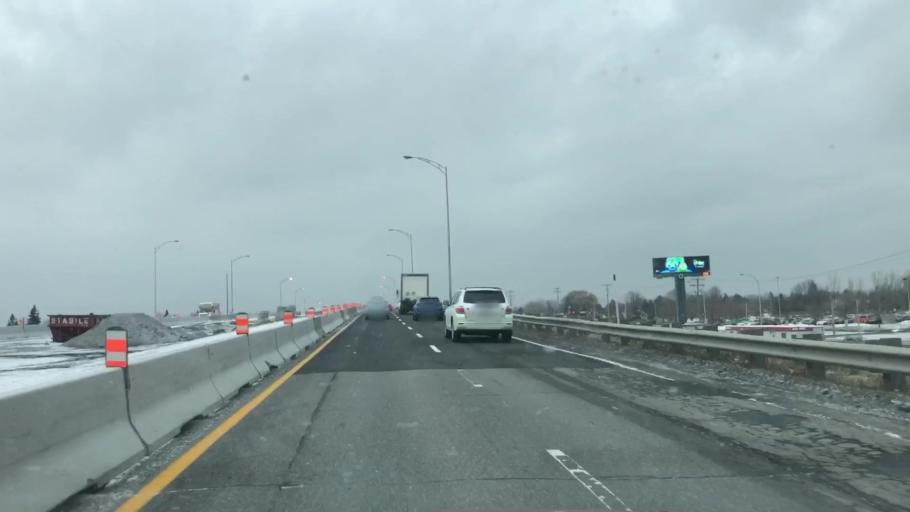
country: CA
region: Quebec
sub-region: Monteregie
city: Brossard
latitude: 45.4546
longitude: -73.4440
